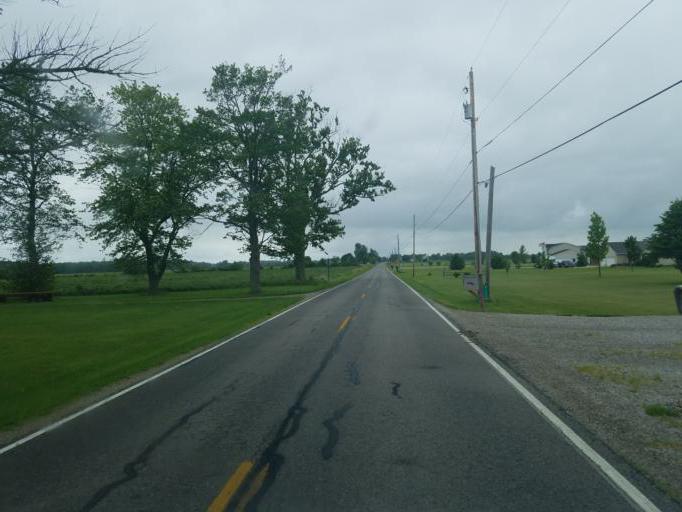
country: US
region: Ohio
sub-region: Marion County
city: Marion
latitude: 40.5644
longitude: -83.0160
